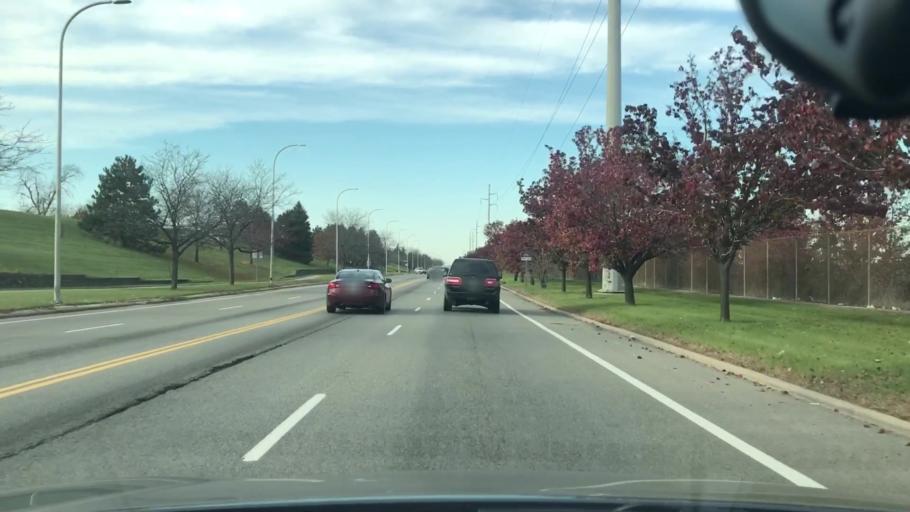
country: US
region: Michigan
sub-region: Wayne County
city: Grosse Pointe Park
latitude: 42.3721
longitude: -82.9739
